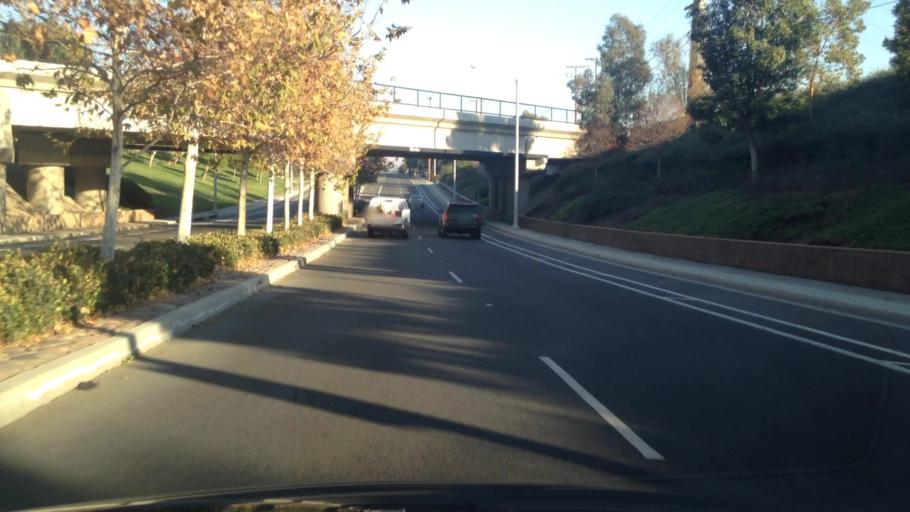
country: US
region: California
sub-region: Riverside County
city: Riverside
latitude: 33.9627
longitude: -117.4299
